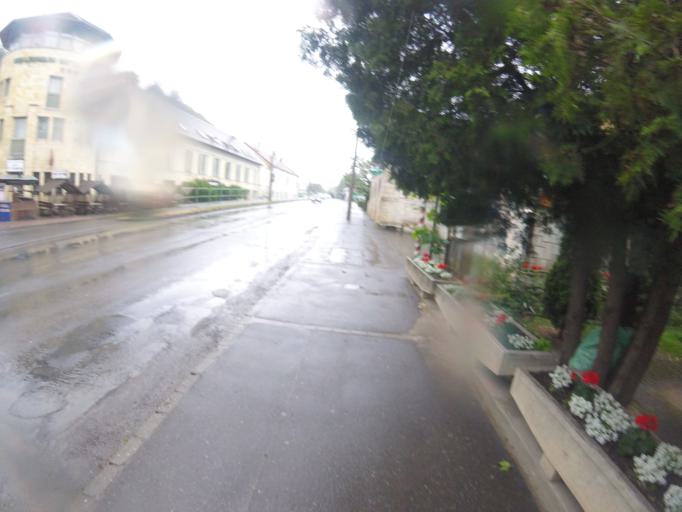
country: HU
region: Borsod-Abauj-Zemplen
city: Tokaj
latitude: 48.1201
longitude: 21.4126
